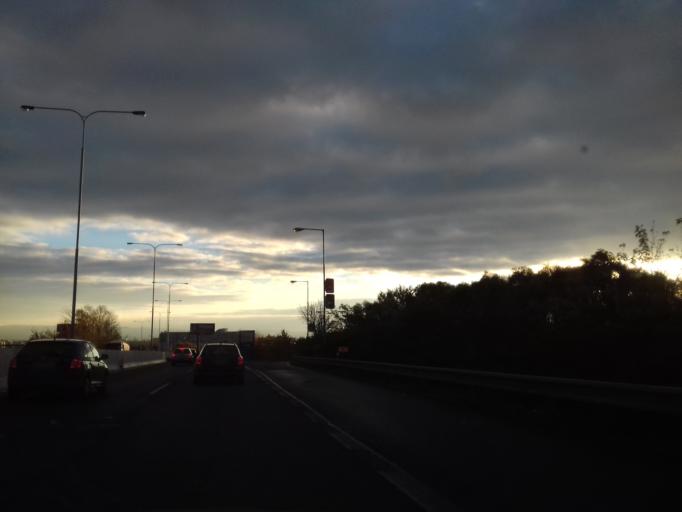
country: CZ
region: Olomoucky
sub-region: Okres Olomouc
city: Olomouc
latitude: 49.5720
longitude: 17.2271
